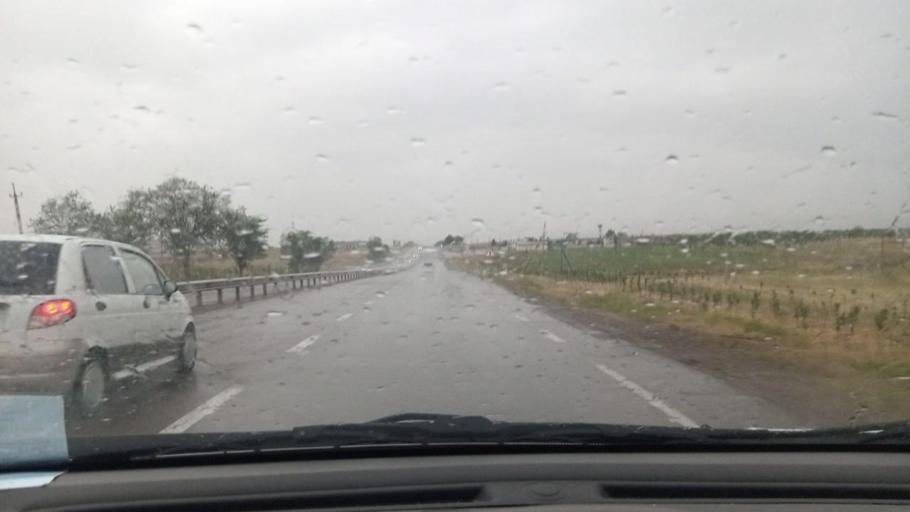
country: UZ
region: Toshkent
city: Ohangaron
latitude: 40.9460
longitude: 69.5759
